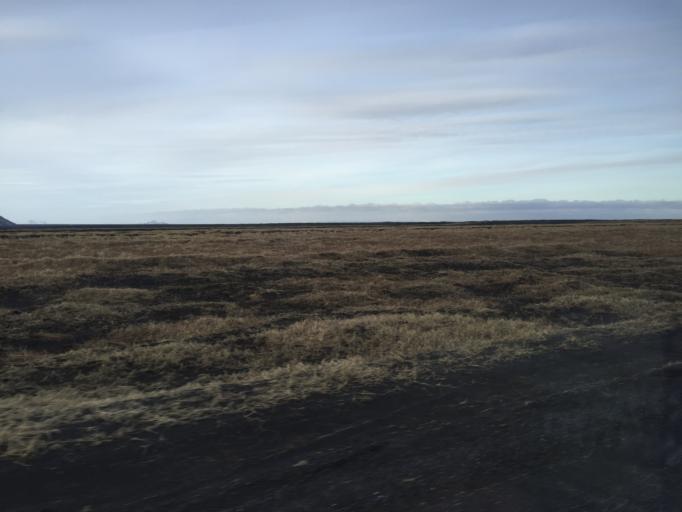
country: IS
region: South
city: Vestmannaeyjar
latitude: 63.4444
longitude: -18.7238
